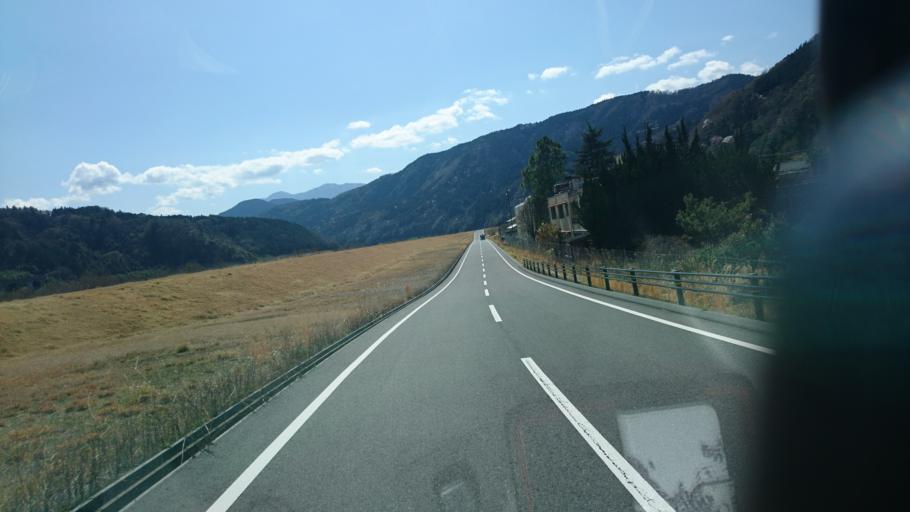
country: JP
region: Shizuoka
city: Fujinomiya
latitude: 35.3631
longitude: 138.4494
